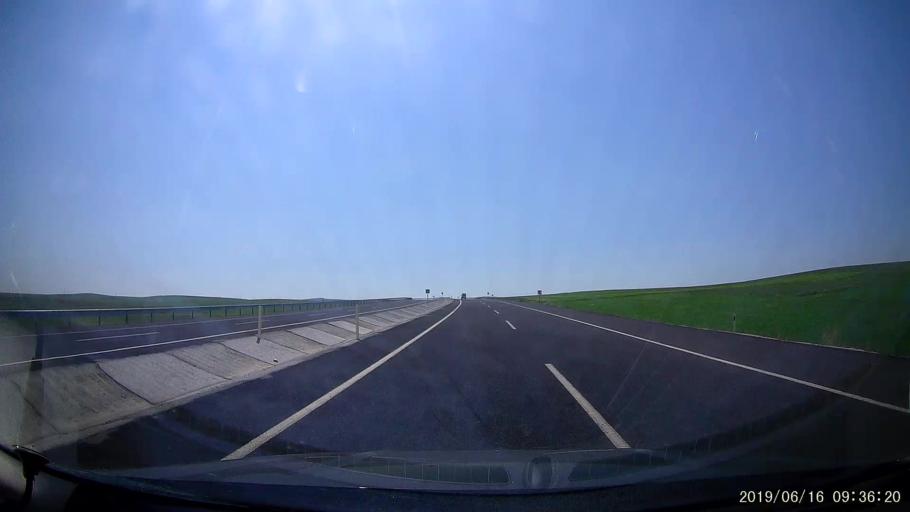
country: TR
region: Kars
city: Kars
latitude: 40.5591
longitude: 43.1702
